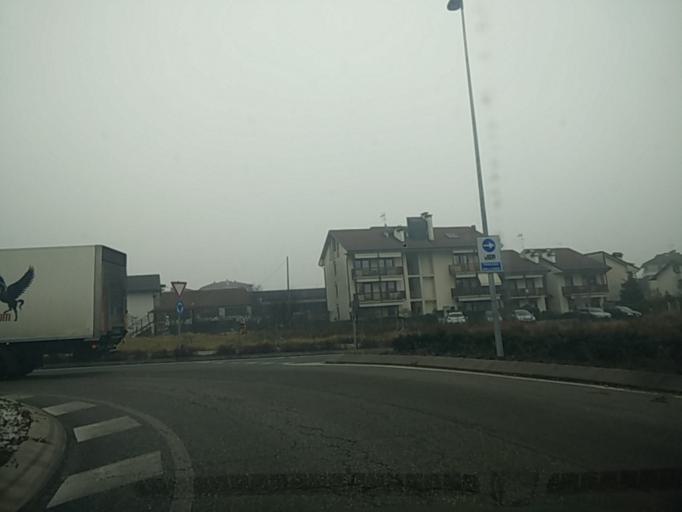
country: IT
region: Veneto
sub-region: Provincia di Belluno
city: Feltre
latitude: 46.0184
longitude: 11.8880
